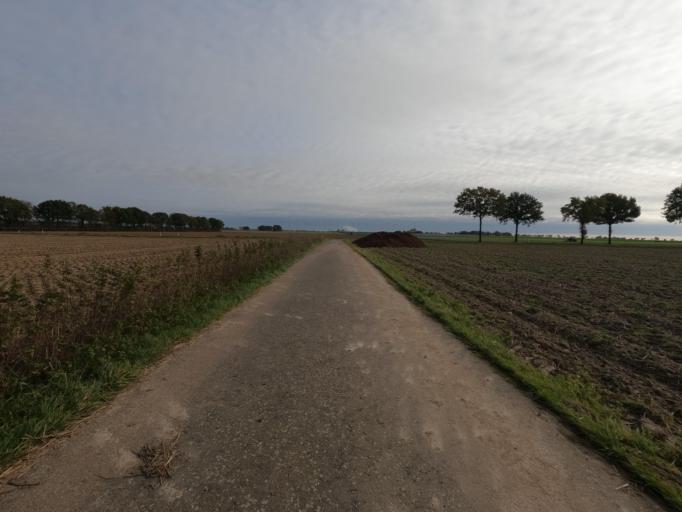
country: DE
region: North Rhine-Westphalia
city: Erkelenz
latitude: 51.0472
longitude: 6.3487
